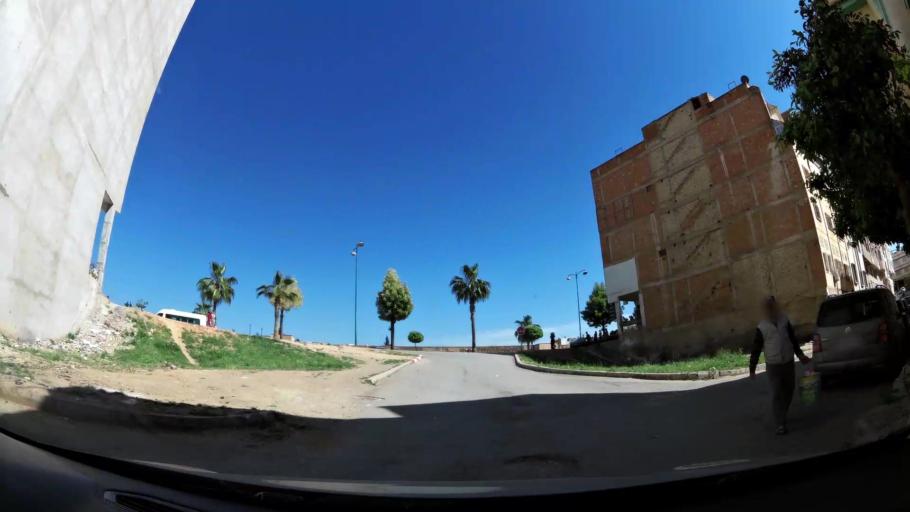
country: MA
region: Meknes-Tafilalet
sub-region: Meknes
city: Meknes
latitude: 33.8825
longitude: -5.5722
